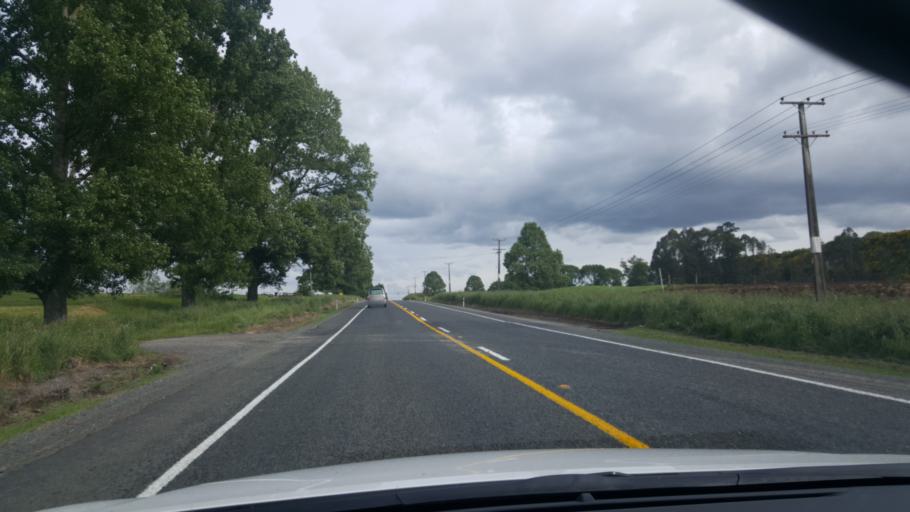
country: NZ
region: Waikato
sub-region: Taupo District
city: Taupo
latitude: -38.4946
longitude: 176.2944
